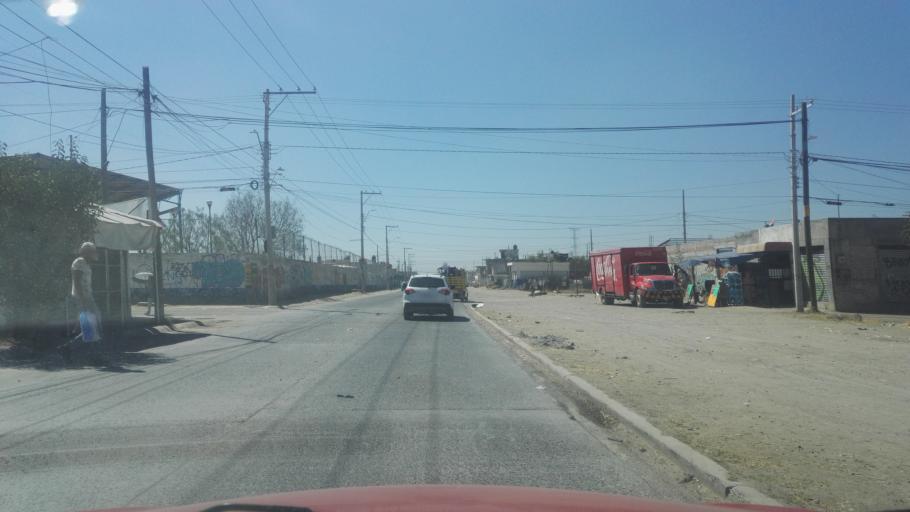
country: MX
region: Guanajuato
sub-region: Leon
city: Fraccionamiento Paraiso Real
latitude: 21.0937
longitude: -101.5918
